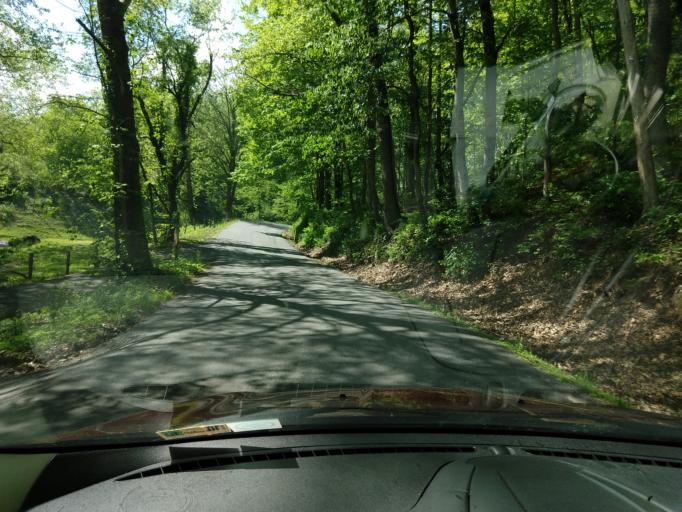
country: US
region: Virginia
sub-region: City of Covington
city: Fairlawn
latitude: 37.7148
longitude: -79.9124
